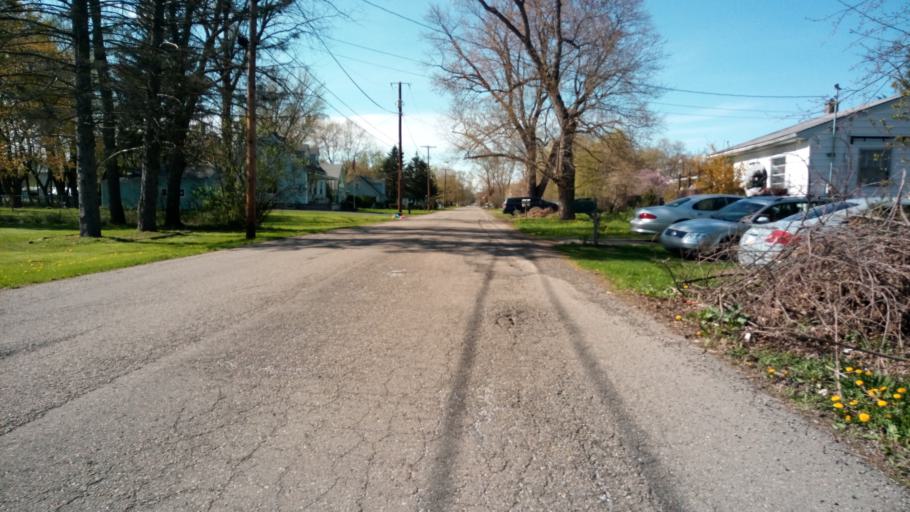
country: US
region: New York
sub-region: Chemung County
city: Southport
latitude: 42.0585
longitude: -76.7945
